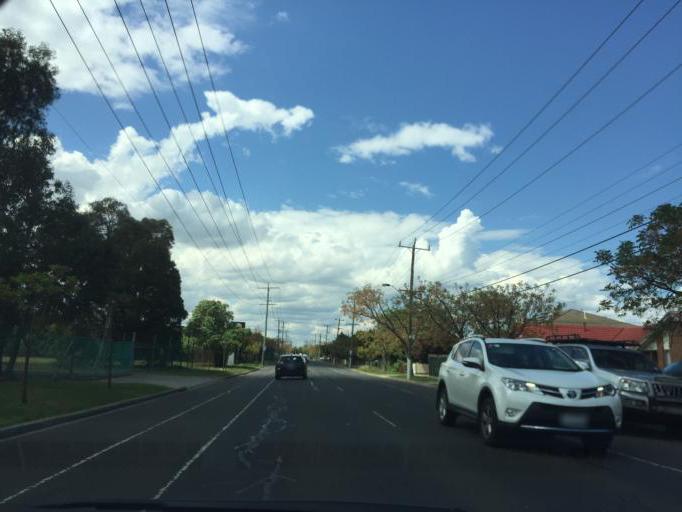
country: AU
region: Victoria
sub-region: Maribyrnong
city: Maidstone
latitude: -37.7823
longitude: 144.8776
